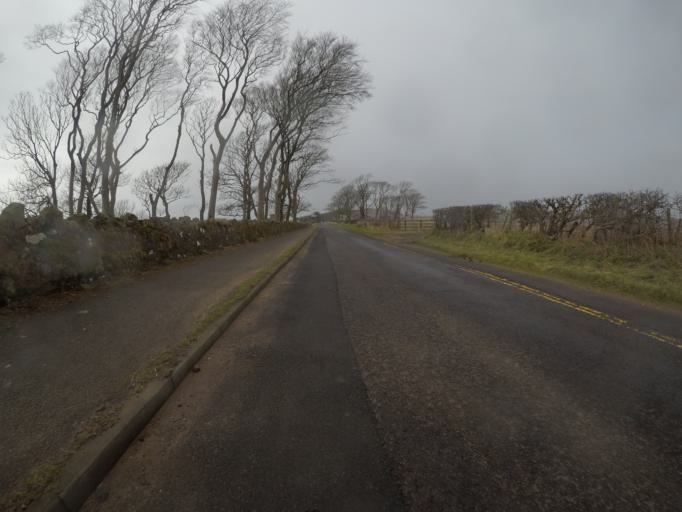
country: GB
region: Scotland
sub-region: North Ayrshire
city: West Kilbride
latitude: 55.6963
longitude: -4.8805
